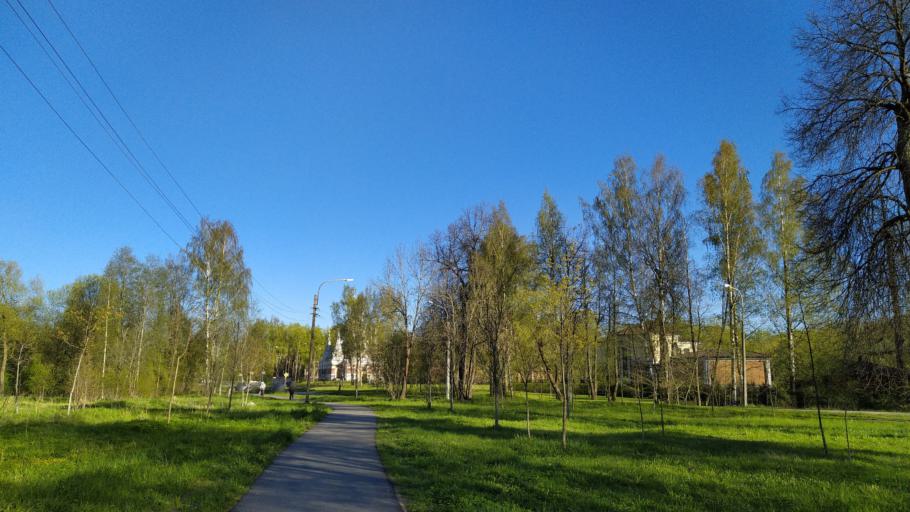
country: RU
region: St.-Petersburg
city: Pavlovsk
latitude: 59.6798
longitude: 30.4472
